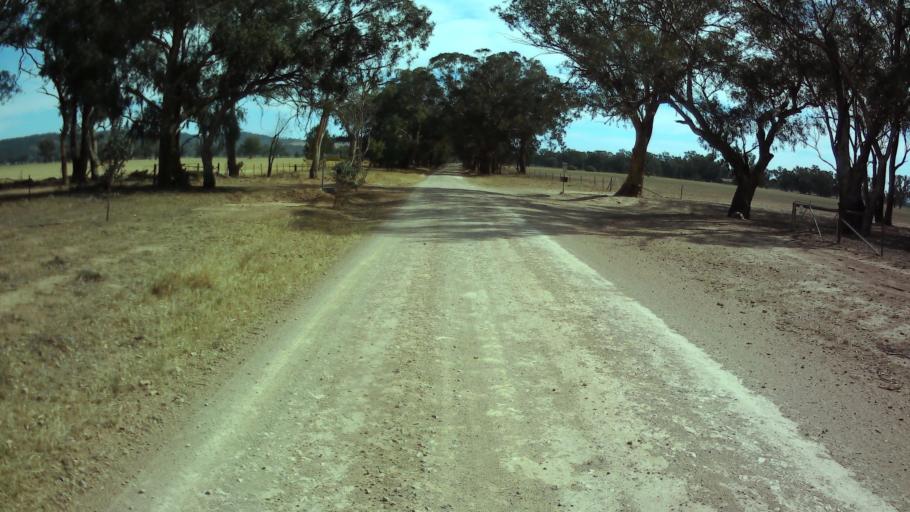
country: AU
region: New South Wales
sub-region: Weddin
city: Grenfell
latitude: -33.6998
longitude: 148.3023
